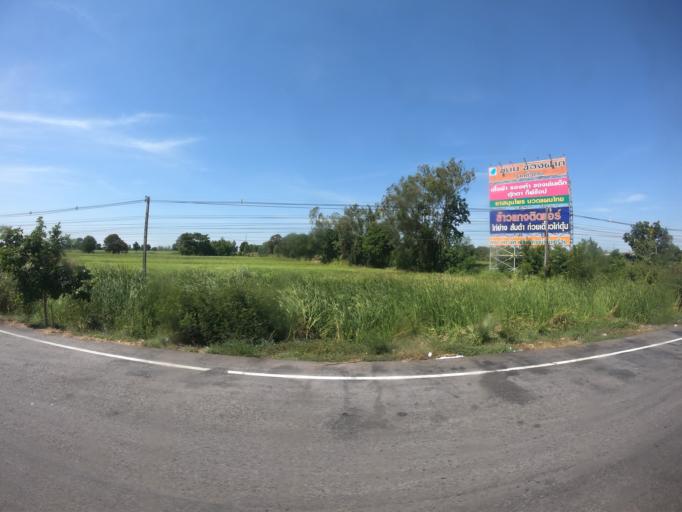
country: TH
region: Khon Kaen
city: Phon
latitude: 15.7221
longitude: 102.5921
